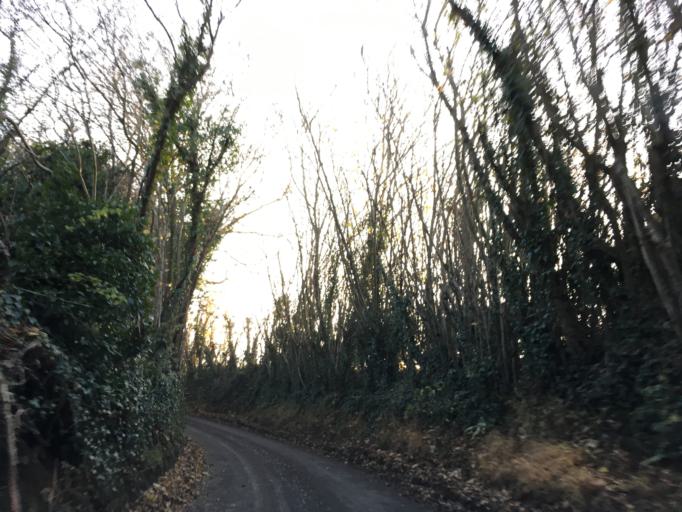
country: GB
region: England
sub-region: Wiltshire
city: Nettleton
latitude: 51.4901
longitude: -2.2579
